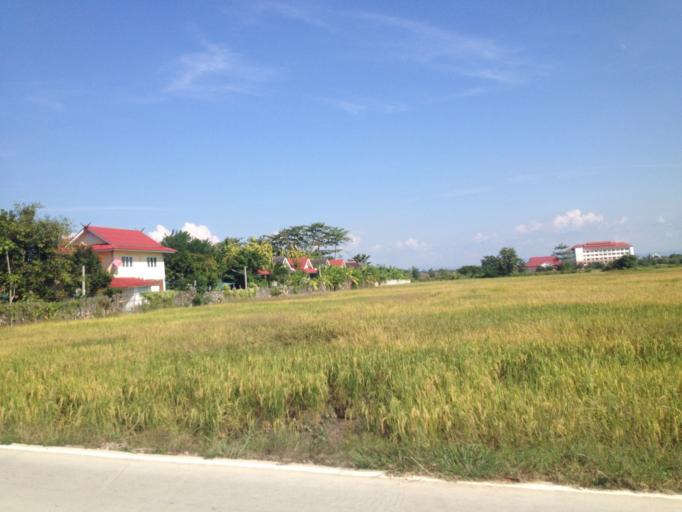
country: TH
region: Chiang Mai
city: Hang Dong
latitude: 18.7129
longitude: 98.9680
